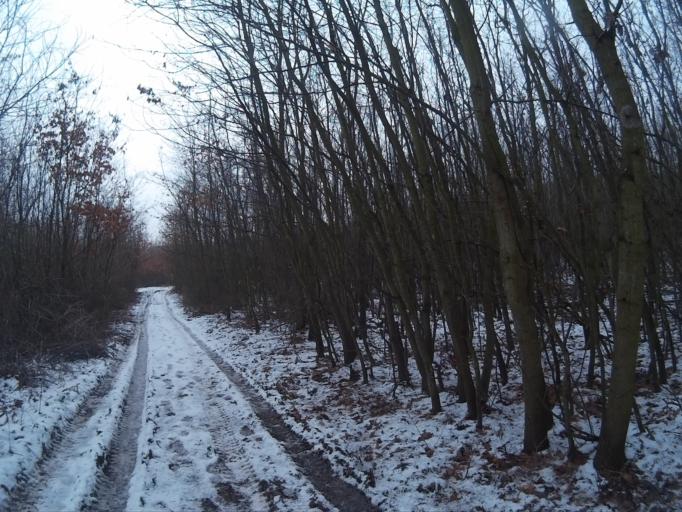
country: HU
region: Komarom-Esztergom
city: Tarjan
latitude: 47.5867
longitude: 18.5158
